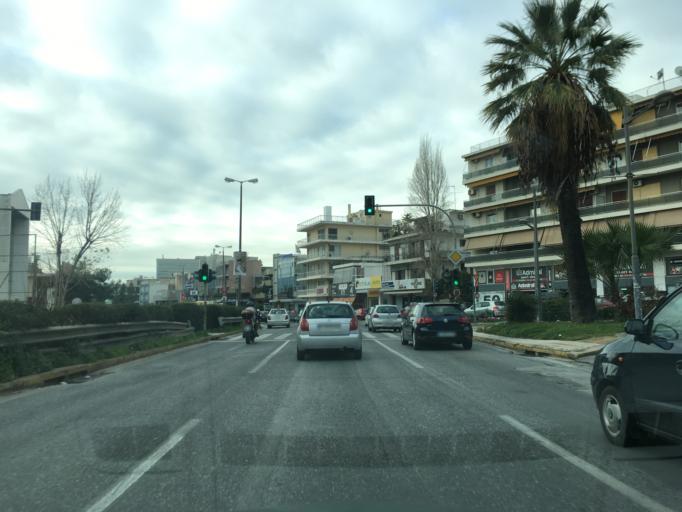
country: GR
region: Attica
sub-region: Nomarchia Athinas
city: Marousi
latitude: 38.0504
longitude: 23.8092
